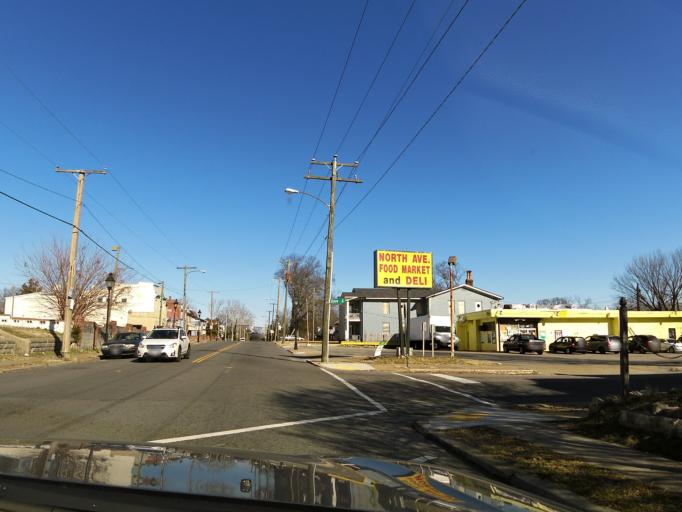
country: US
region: Virginia
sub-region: City of Richmond
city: Richmond
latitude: 37.5634
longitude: -77.4333
